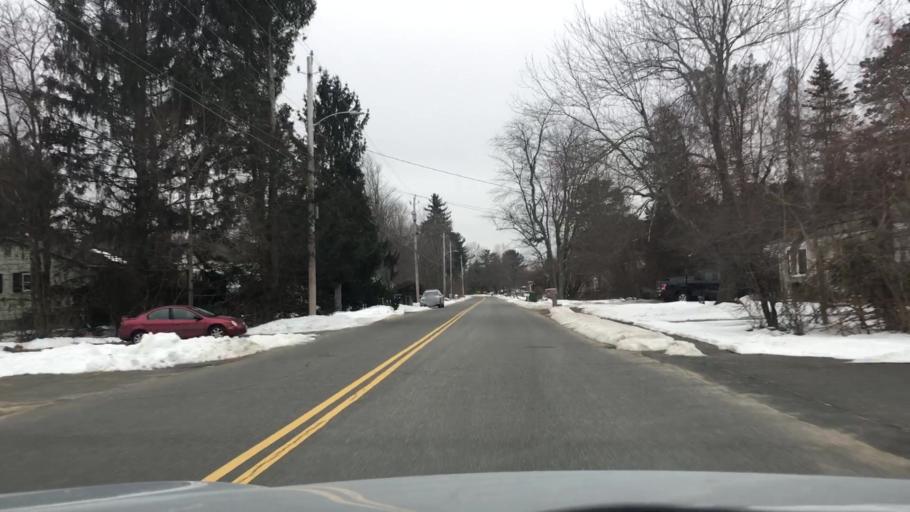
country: US
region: Massachusetts
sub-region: Hampshire County
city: Southampton
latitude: 42.1816
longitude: -72.6827
